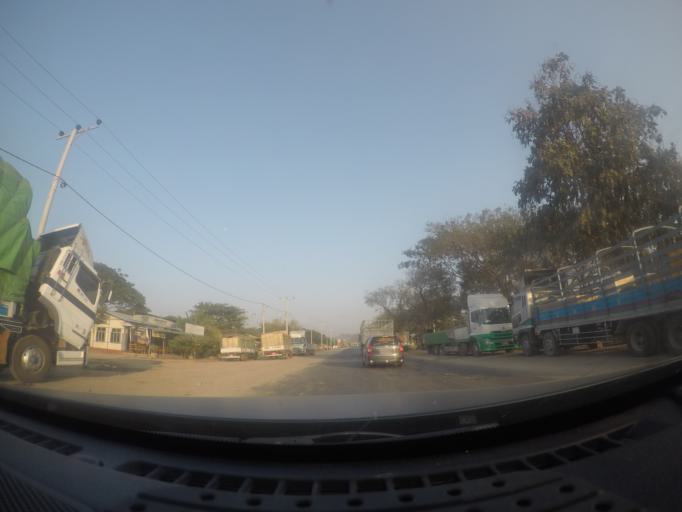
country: MM
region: Mandalay
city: Yamethin
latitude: 20.7544
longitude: 96.2538
